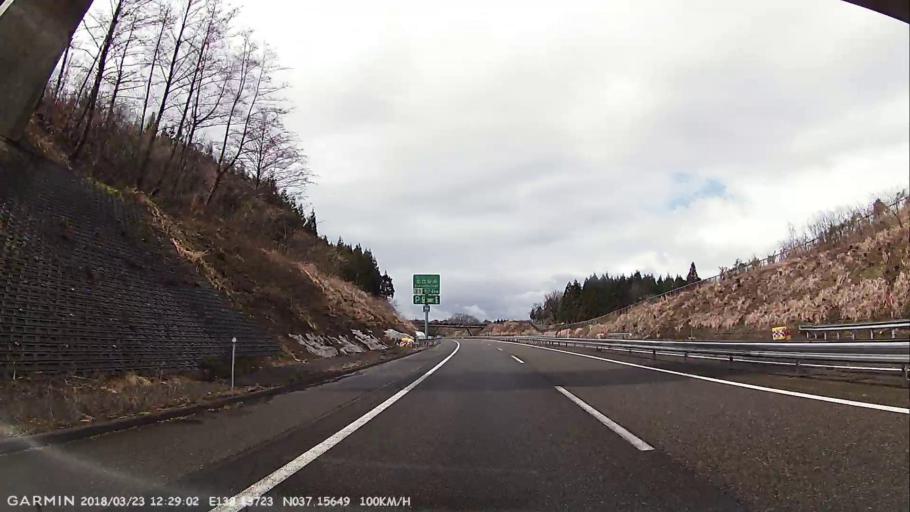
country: JP
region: Niigata
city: Joetsu
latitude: 37.1566
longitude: 138.1371
